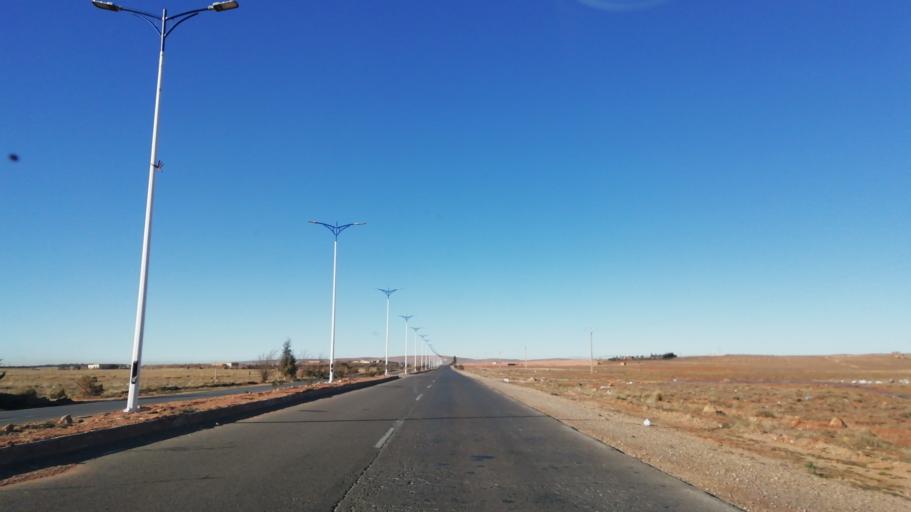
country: DZ
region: El Bayadh
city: El Bayadh
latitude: 33.6898
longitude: 1.0667
